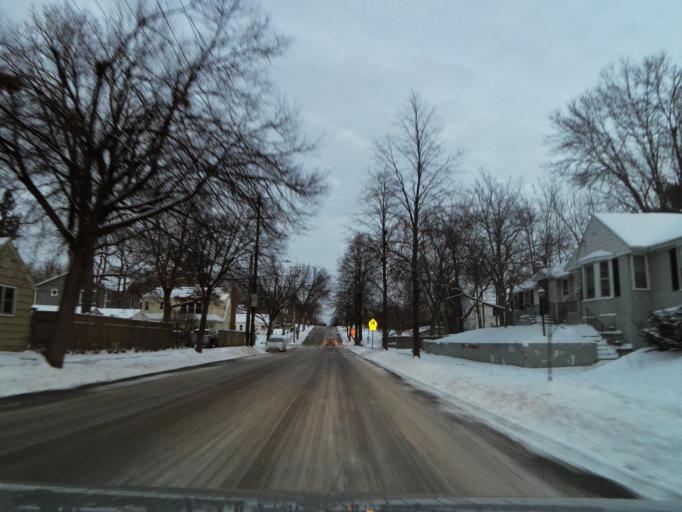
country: US
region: Minnesota
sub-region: Hennepin County
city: Richfield
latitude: 44.9016
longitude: -93.3138
